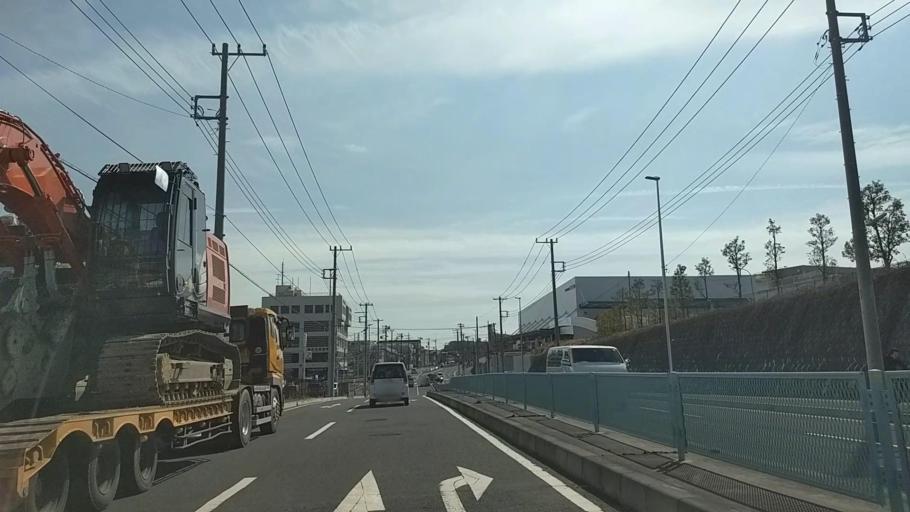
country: JP
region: Kanagawa
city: Fujisawa
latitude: 35.3970
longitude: 139.4570
